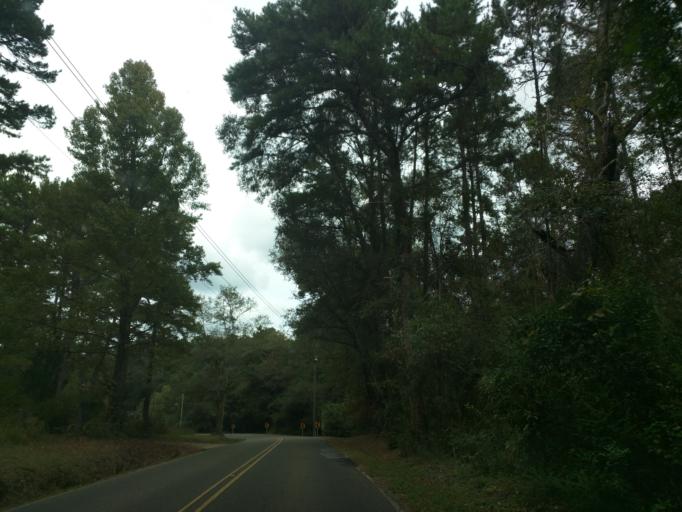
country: US
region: Florida
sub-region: Leon County
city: Tallahassee
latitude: 30.4253
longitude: -84.2101
